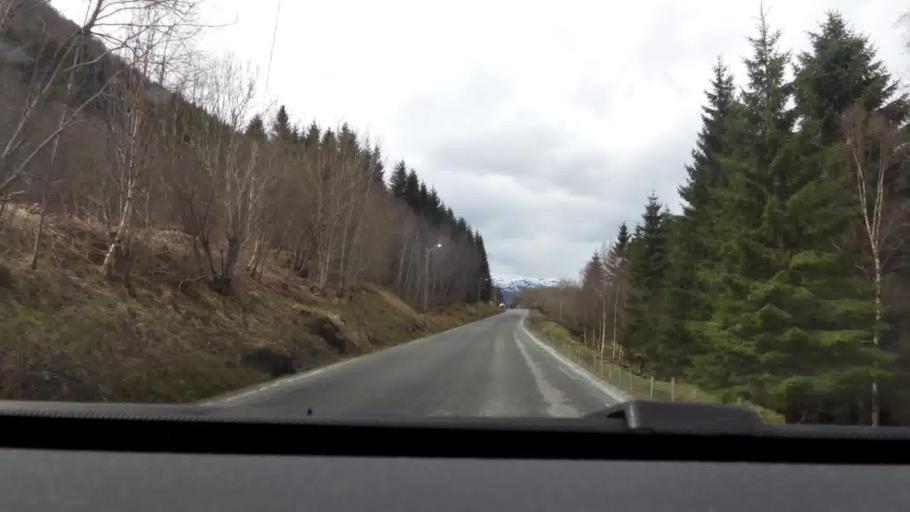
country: NO
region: More og Romsdal
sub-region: Gjemnes
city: Batnfjordsora
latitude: 62.9246
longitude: 7.5852
